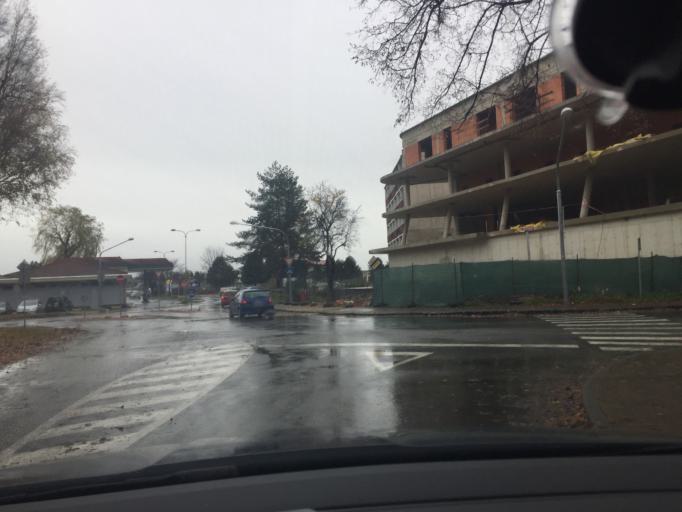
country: SK
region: Presovsky
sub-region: Okres Presov
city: Kezmarok
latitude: 49.1408
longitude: 20.4327
